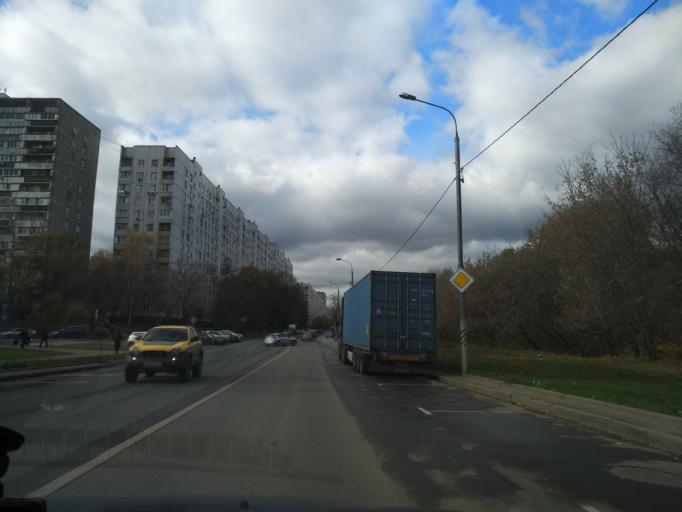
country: RU
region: Moscow
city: Bibirevo
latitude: 55.8988
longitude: 37.6246
